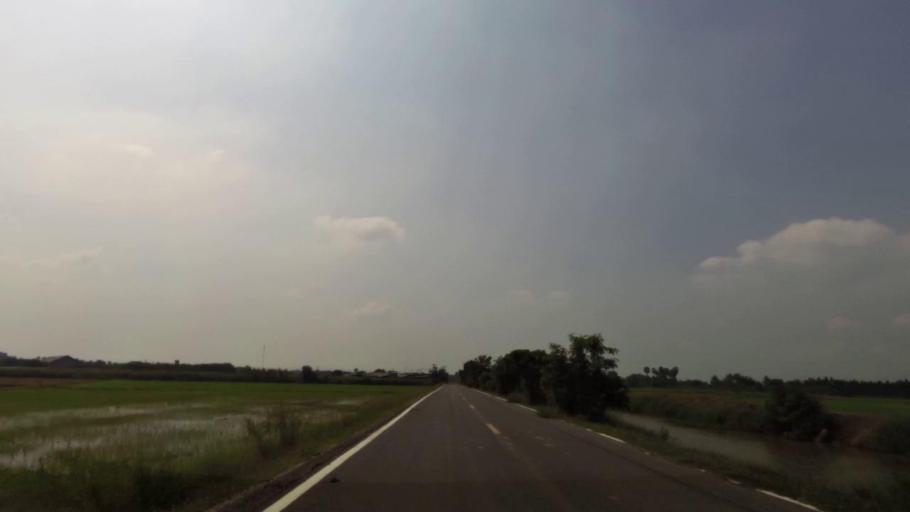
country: TH
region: Ang Thong
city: Pho Thong
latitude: 14.6145
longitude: 100.3995
